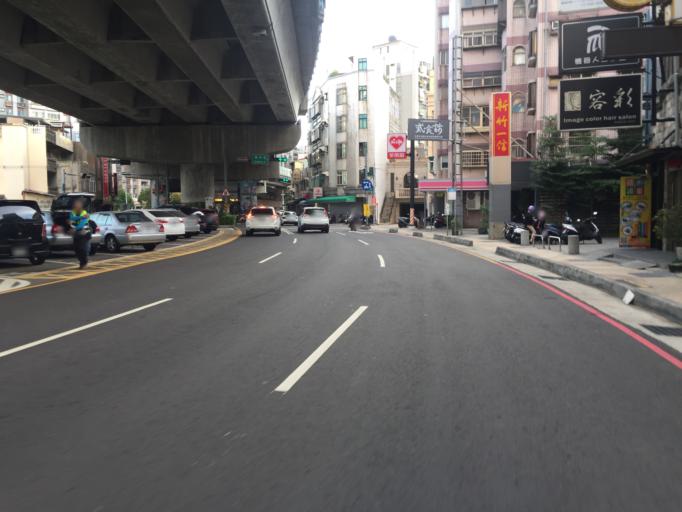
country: TW
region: Taiwan
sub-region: Hsinchu
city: Hsinchu
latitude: 24.8201
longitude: 120.9673
